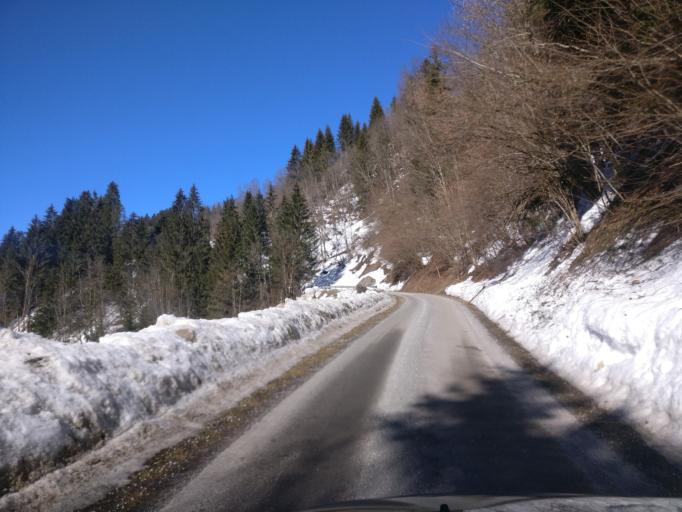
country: AT
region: Salzburg
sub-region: Politischer Bezirk Sankt Johann im Pongau
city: Wagrain
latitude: 47.3346
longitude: 13.2604
